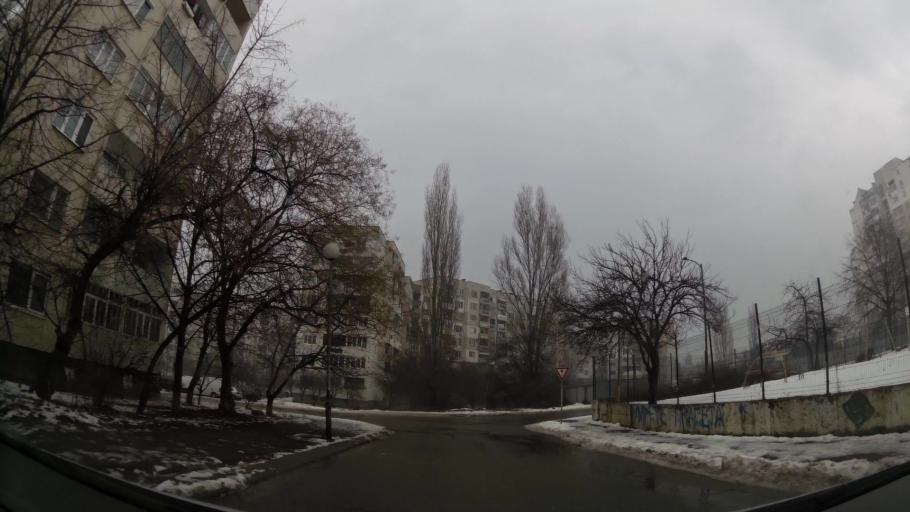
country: BG
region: Sofiya
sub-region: Obshtina Bozhurishte
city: Bozhurishte
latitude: 42.6876
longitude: 23.2438
